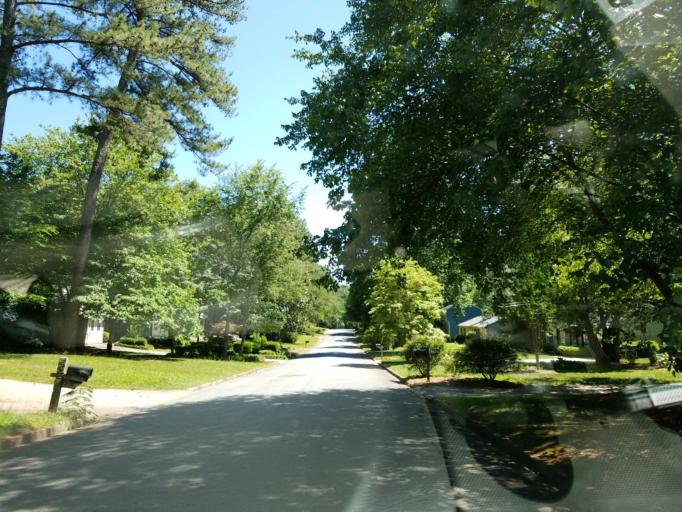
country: US
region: Georgia
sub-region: Cobb County
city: Marietta
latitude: 33.9628
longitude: -84.4683
